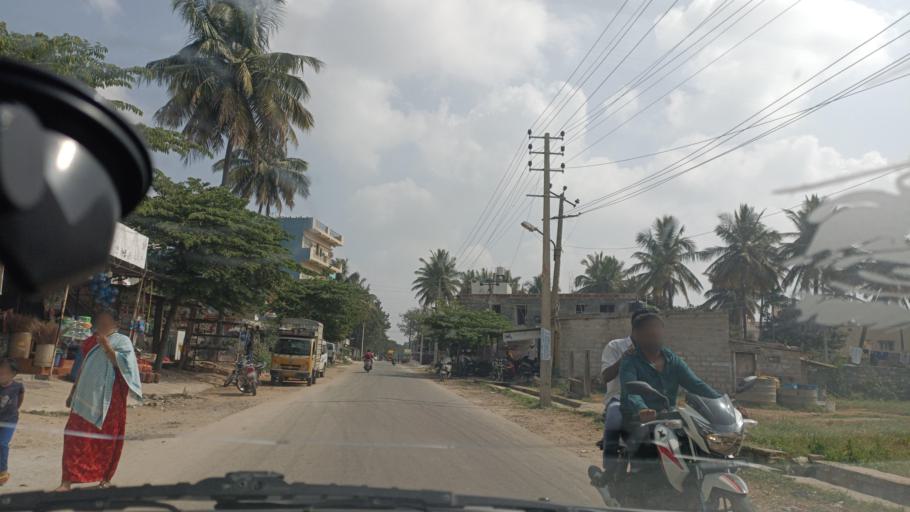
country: IN
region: Karnataka
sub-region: Bangalore Urban
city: Yelahanka
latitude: 13.1564
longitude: 77.6195
